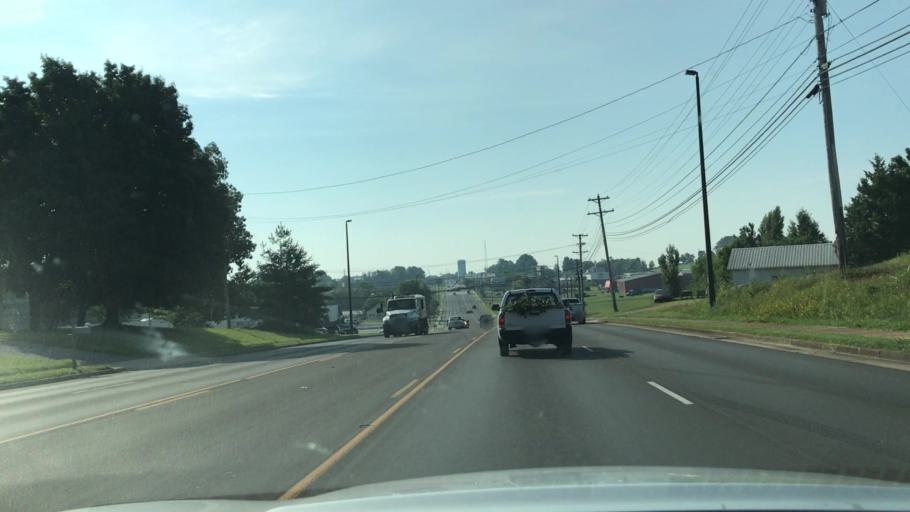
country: US
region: Kentucky
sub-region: Barren County
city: Glasgow
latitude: 37.0058
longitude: -85.9326
